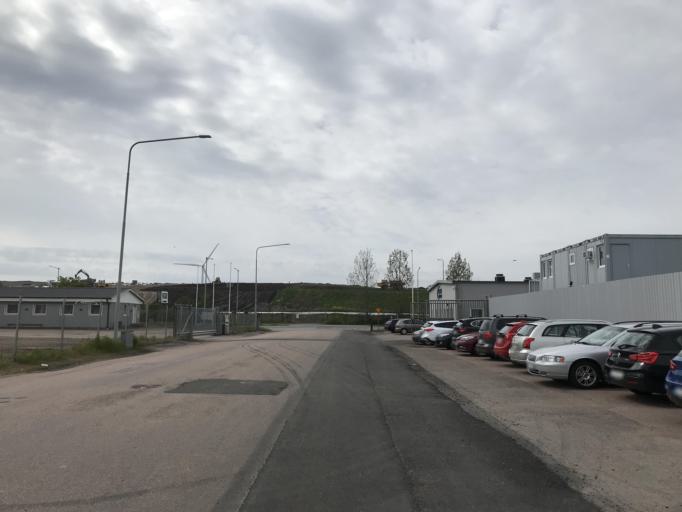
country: SE
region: Skane
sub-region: Landskrona
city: Landskrona
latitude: 55.8660
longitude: 12.8625
